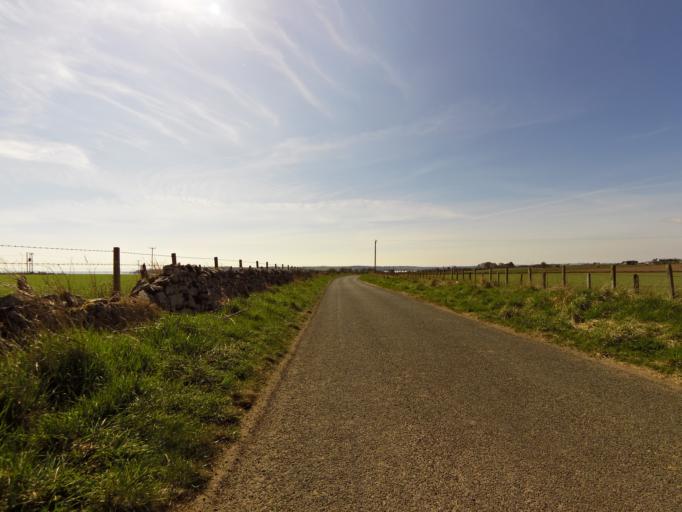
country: GB
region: Scotland
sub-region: Angus
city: Montrose
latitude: 56.6710
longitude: -2.4994
